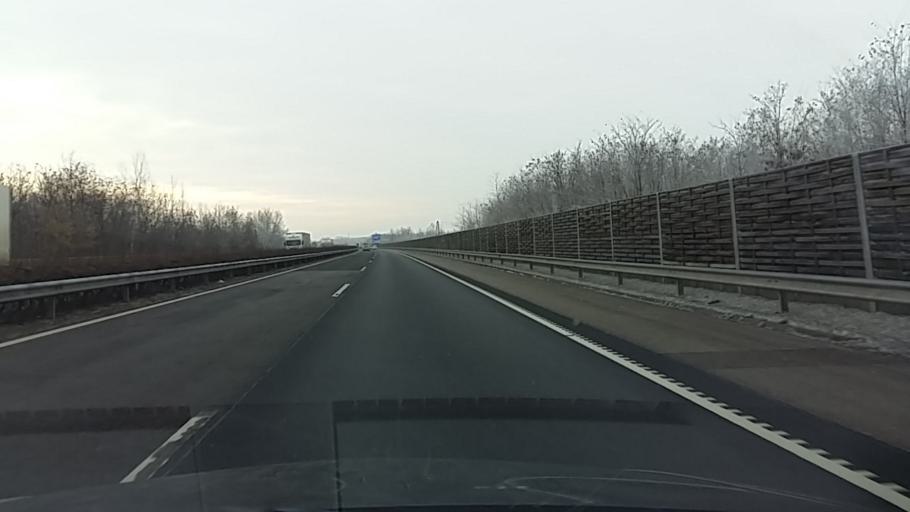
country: HU
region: Bacs-Kiskun
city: Balloszog
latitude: 46.9026
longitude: 19.6172
